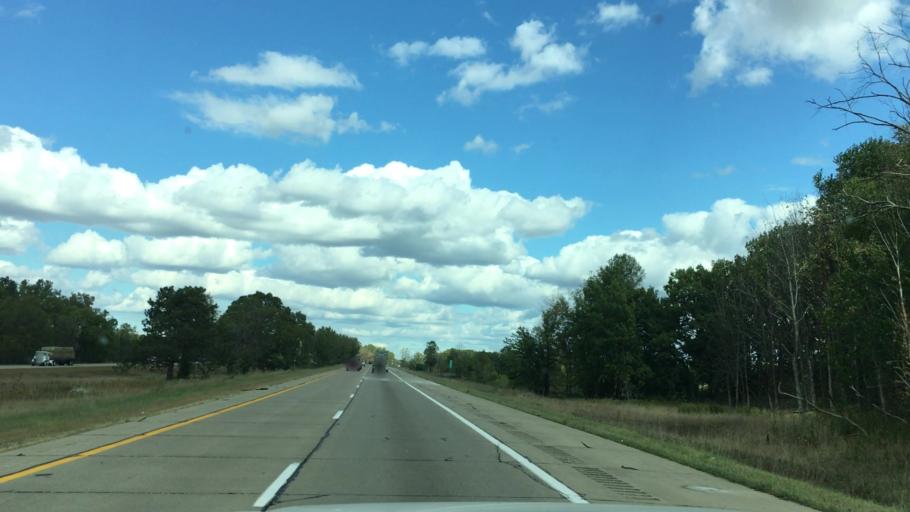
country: US
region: Michigan
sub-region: Eaton County
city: Olivet
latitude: 42.4659
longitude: -84.9016
